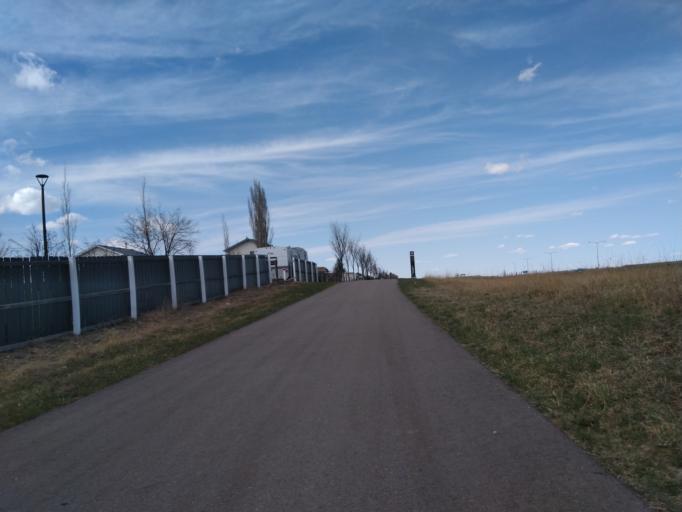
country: CA
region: Alberta
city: Chestermere
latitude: 51.0424
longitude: -113.9228
